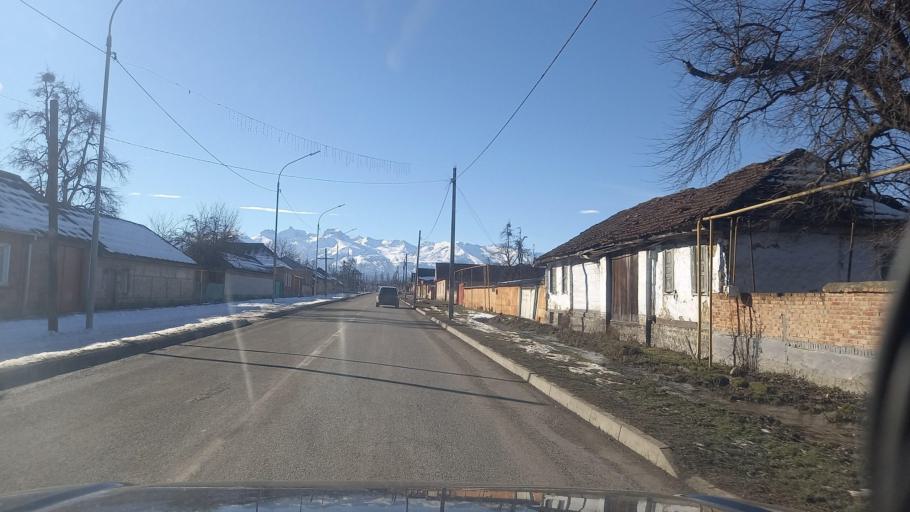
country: RU
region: North Ossetia
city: Chikola
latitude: 43.1916
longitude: 43.9105
